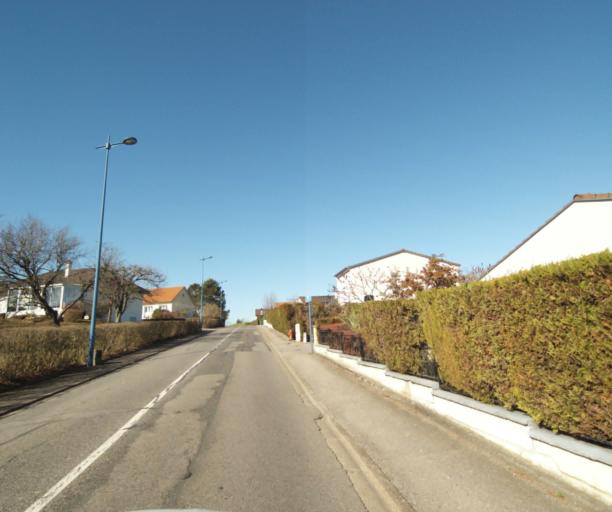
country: FR
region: Lorraine
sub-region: Departement de Meurthe-et-Moselle
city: Heillecourt
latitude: 48.6442
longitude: 6.1994
